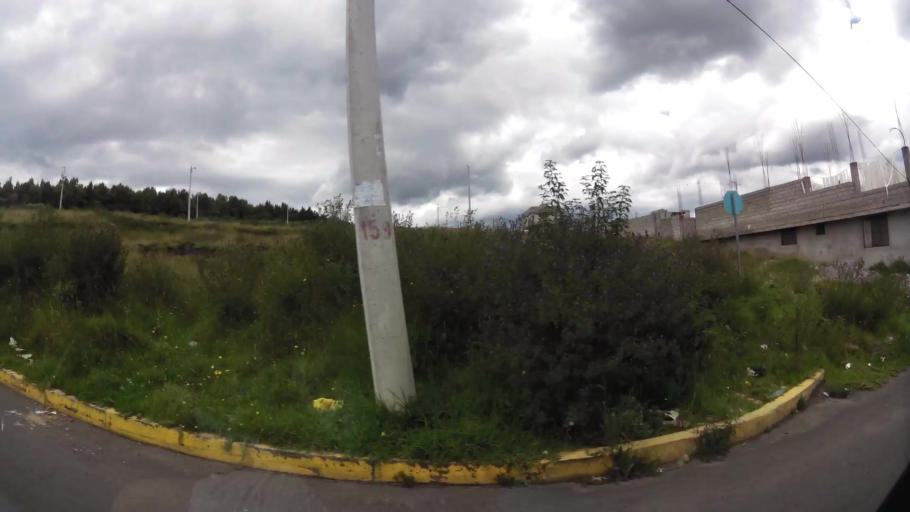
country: EC
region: Pichincha
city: Sangolqui
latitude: -0.3271
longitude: -78.5212
